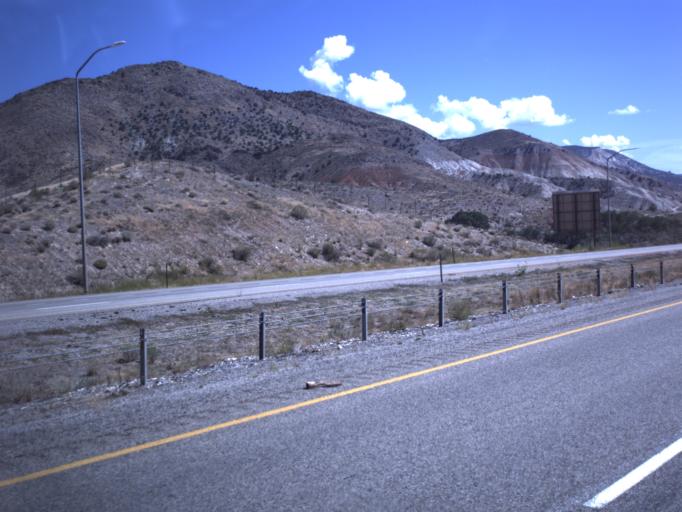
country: US
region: Utah
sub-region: Sevier County
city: Salina
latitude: 38.9327
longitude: -111.8472
